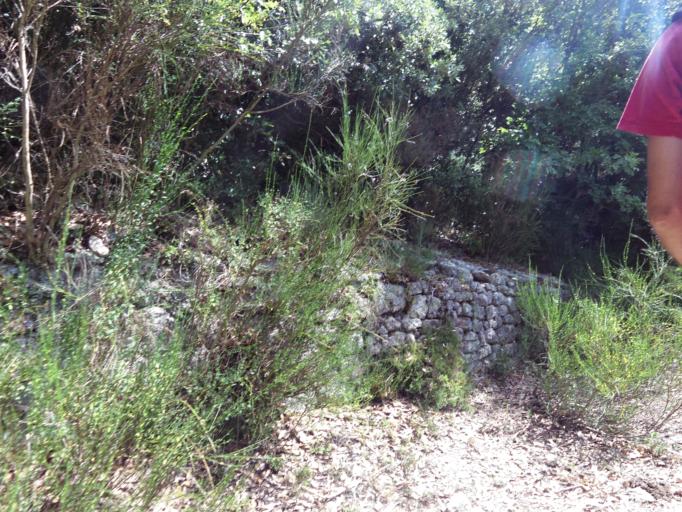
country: IT
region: Calabria
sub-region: Provincia di Vibo-Valentia
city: Nardodipace
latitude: 38.5075
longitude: 16.3874
